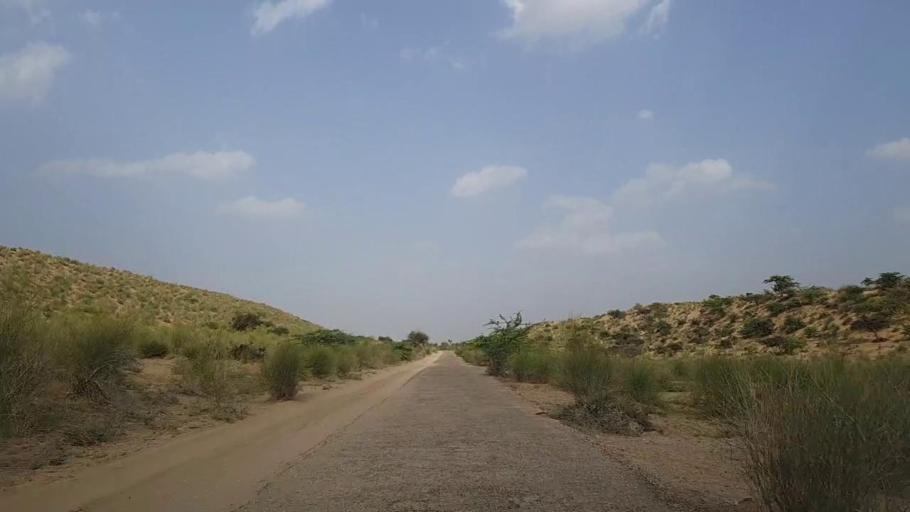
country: PK
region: Sindh
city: Islamkot
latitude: 24.7697
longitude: 70.1755
